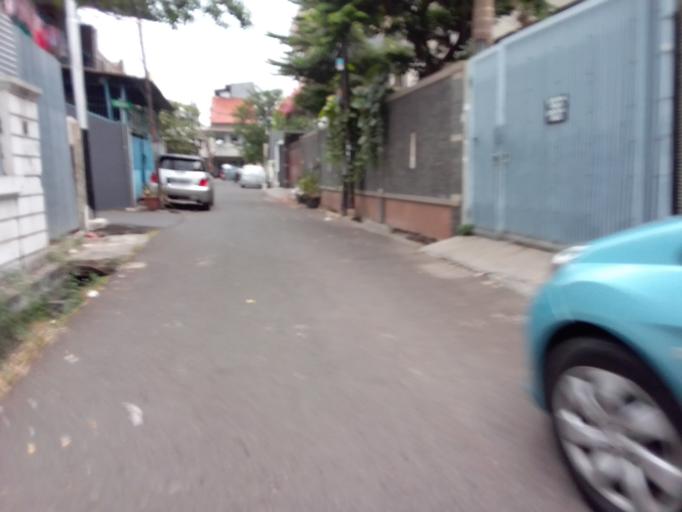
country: ID
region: Jakarta Raya
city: Jakarta
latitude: -6.1740
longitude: 106.8123
